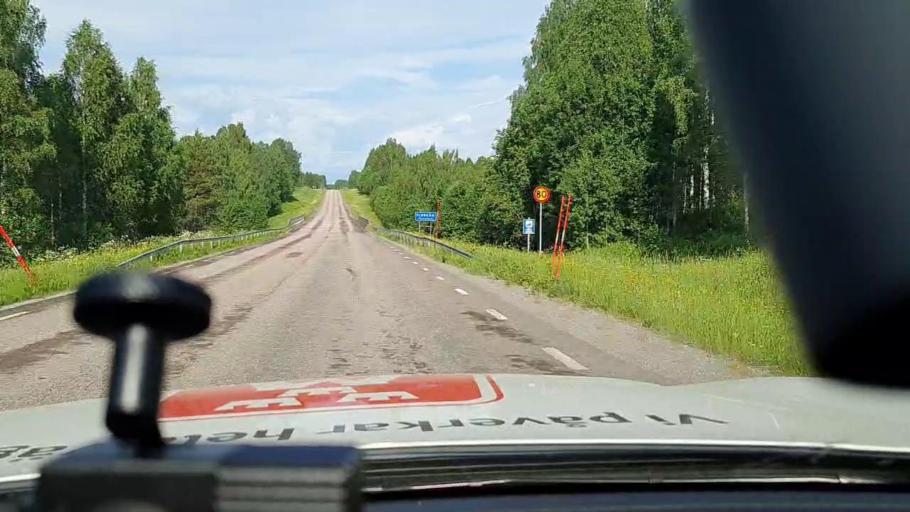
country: SE
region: Norrbotten
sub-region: Alvsbyns Kommun
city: AElvsbyn
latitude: 66.0132
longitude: 21.1698
